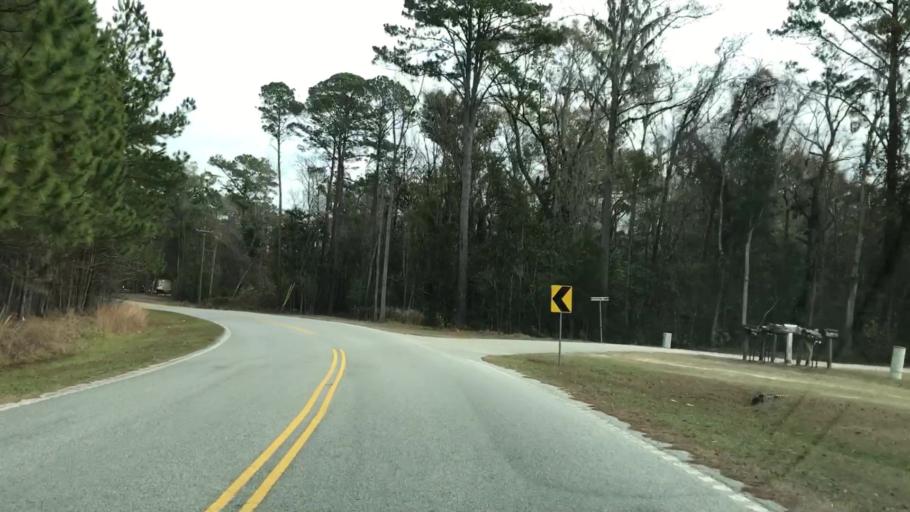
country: US
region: South Carolina
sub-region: Beaufort County
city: Burton
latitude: 32.4173
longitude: -80.7428
